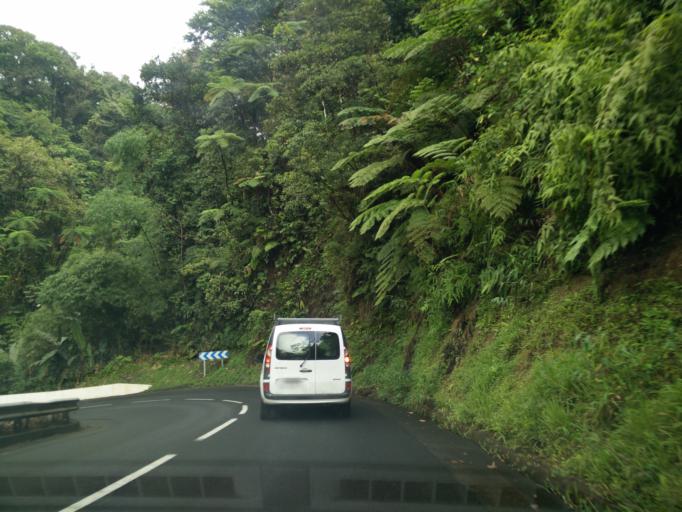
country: MQ
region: Martinique
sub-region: Martinique
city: Saint-Joseph
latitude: 14.7068
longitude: -61.0952
